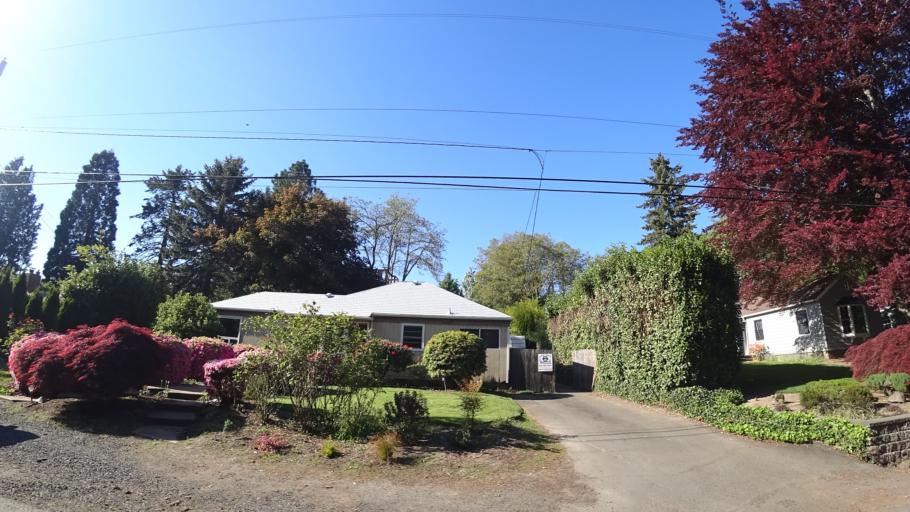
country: US
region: Oregon
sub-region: Washington County
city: West Slope
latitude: 45.4963
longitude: -122.7657
